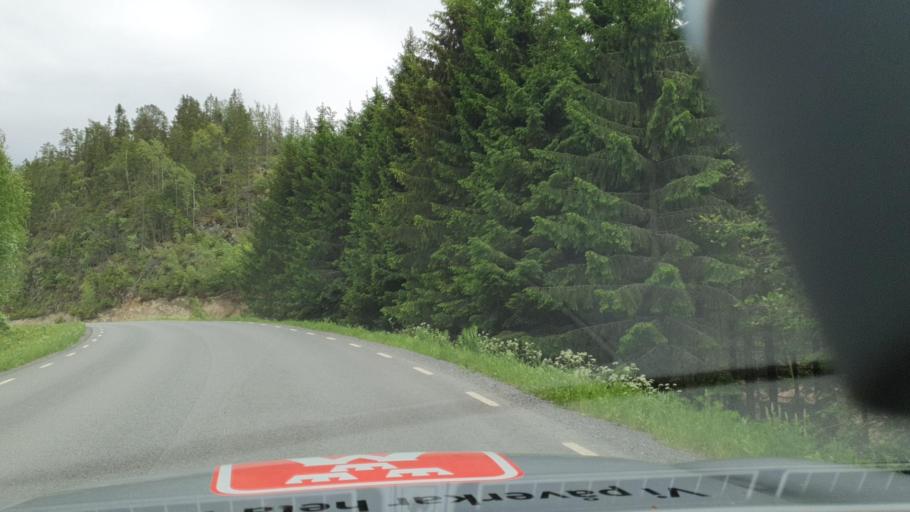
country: SE
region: Vaesternorrland
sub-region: Kramfors Kommun
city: Nordingra
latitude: 62.8983
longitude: 18.3251
